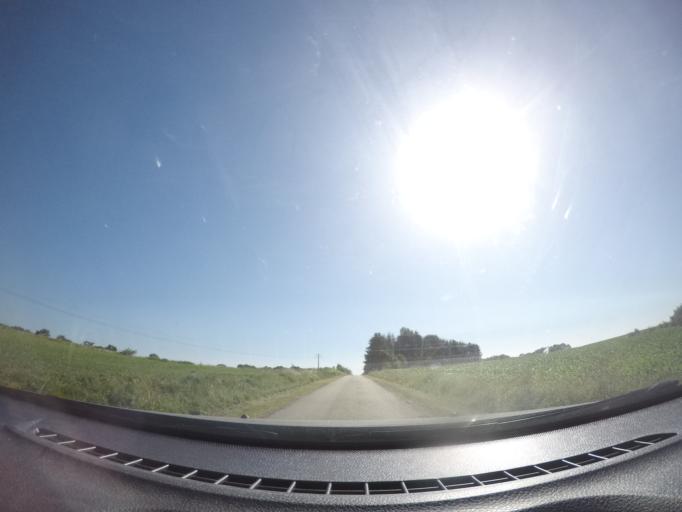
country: BE
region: Wallonia
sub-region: Province de Namur
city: Philippeville
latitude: 50.1871
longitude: 4.6013
